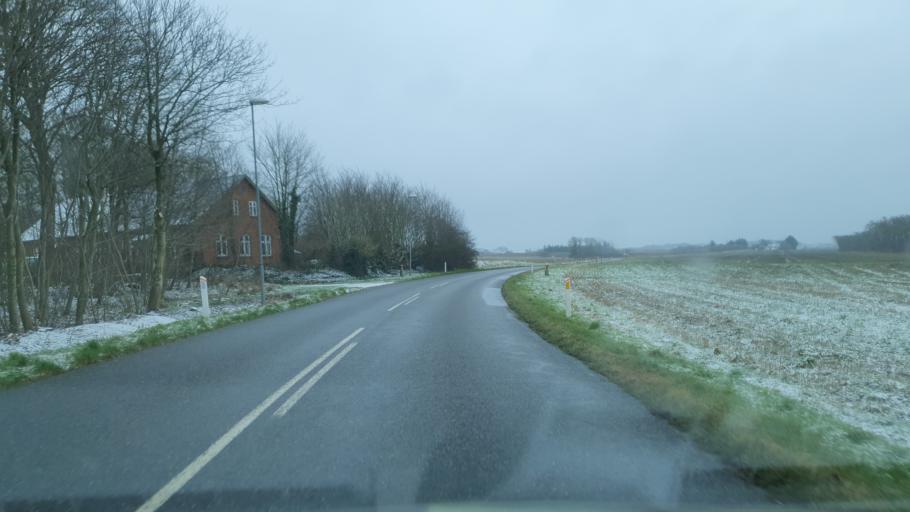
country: DK
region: North Denmark
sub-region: Jammerbugt Kommune
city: Brovst
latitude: 57.1315
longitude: 9.4705
